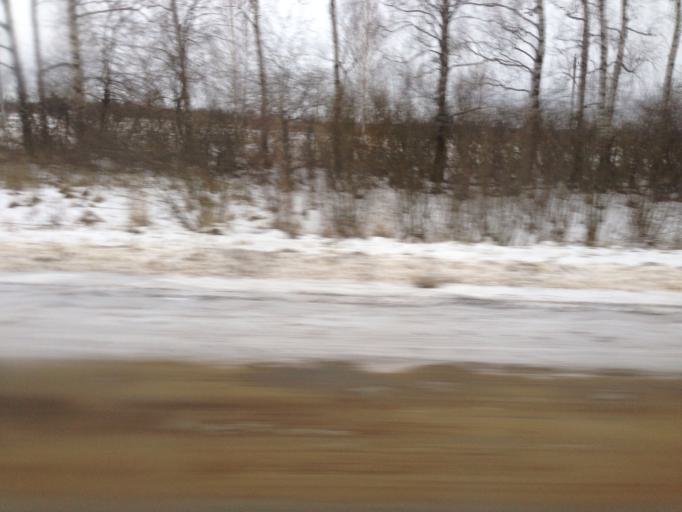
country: RU
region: Tula
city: Bolokhovo
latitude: 54.0583
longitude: 37.8055
